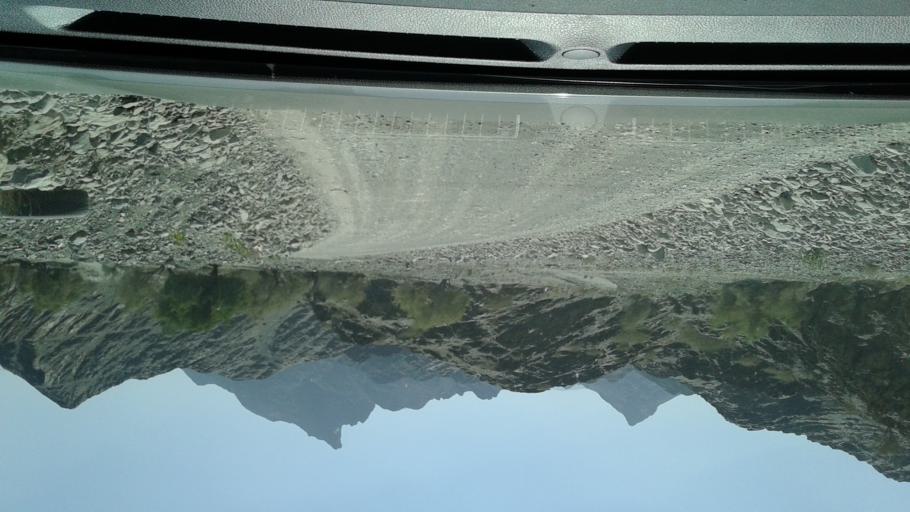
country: OM
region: Al Batinah
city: Bayt al `Awabi
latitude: 23.2636
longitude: 57.4461
